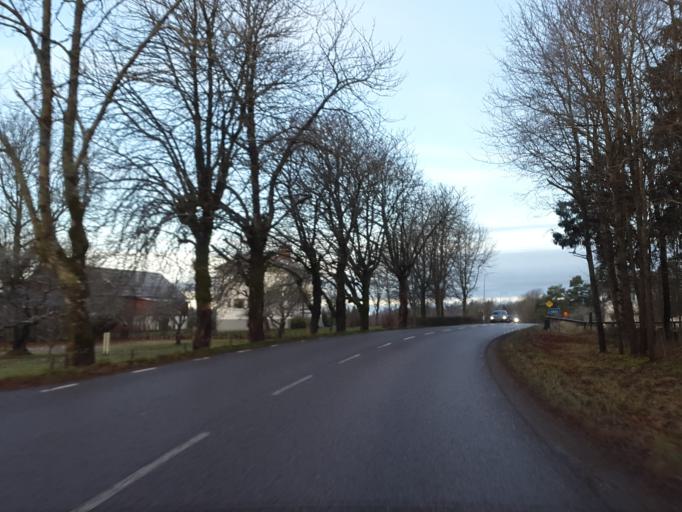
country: SE
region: Vaestra Goetaland
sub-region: Boras Kommun
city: Sjomarken
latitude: 57.7707
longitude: 12.8180
